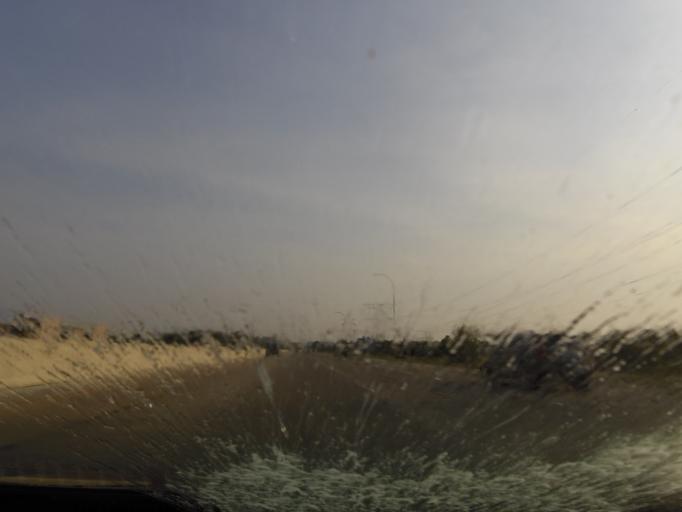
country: US
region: Minnesota
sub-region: Hennepin County
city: Maple Grove
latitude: 45.0778
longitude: -93.4465
